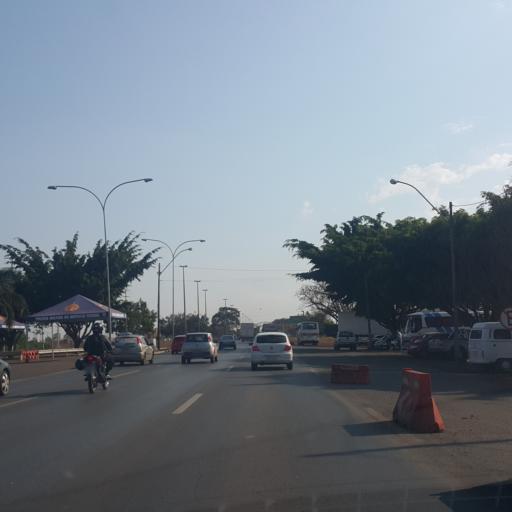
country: BR
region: Federal District
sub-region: Brasilia
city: Brasilia
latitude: -15.8756
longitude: -48.0482
